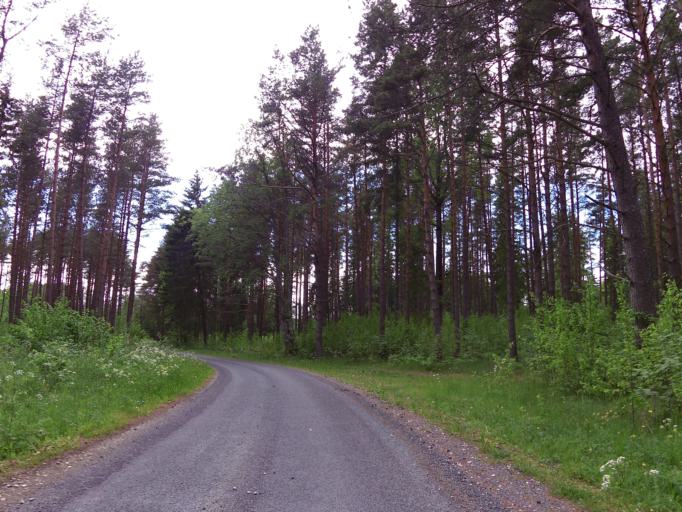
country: EE
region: Harju
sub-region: Paldiski linn
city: Paldiski
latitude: 59.2525
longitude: 23.7602
